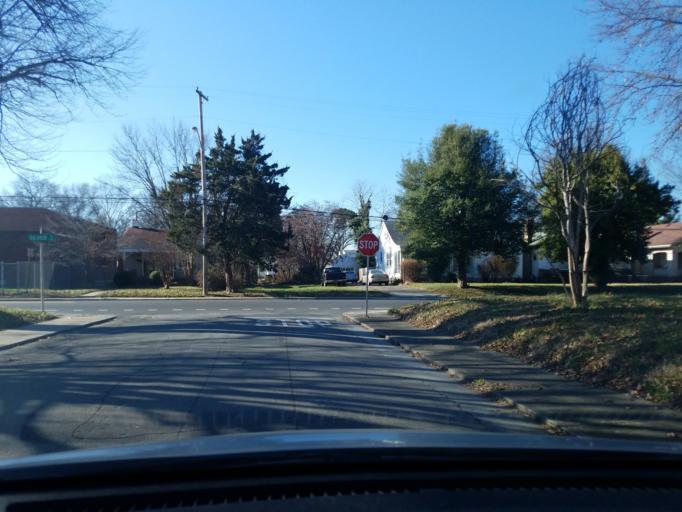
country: US
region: Indiana
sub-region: Floyd County
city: New Albany
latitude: 38.3009
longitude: -85.8036
